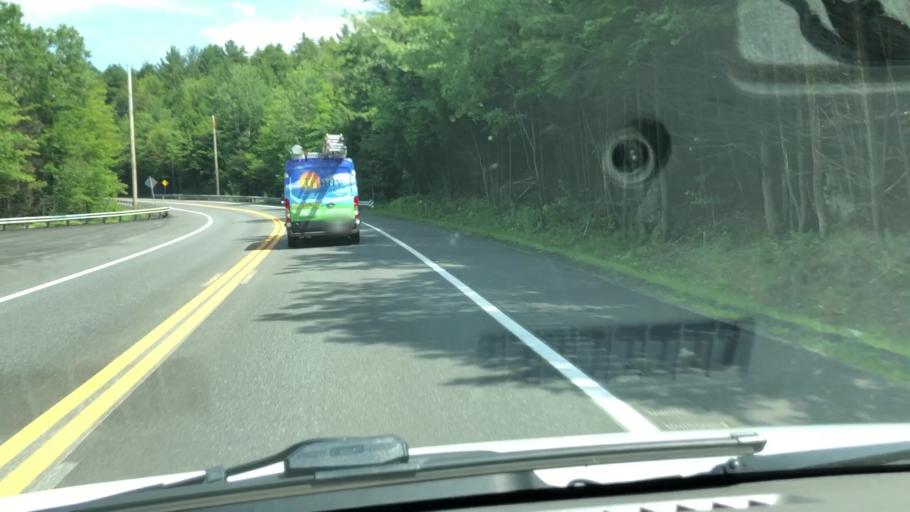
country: US
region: Massachusetts
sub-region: Hampshire County
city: Chesterfield
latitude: 42.4546
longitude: -72.8476
